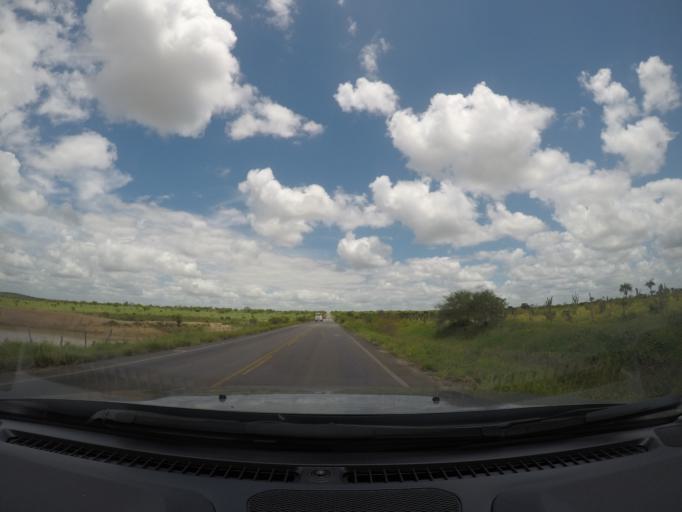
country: BR
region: Bahia
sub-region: Itaberaba
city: Itaberaba
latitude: -12.3550
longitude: -40.0255
